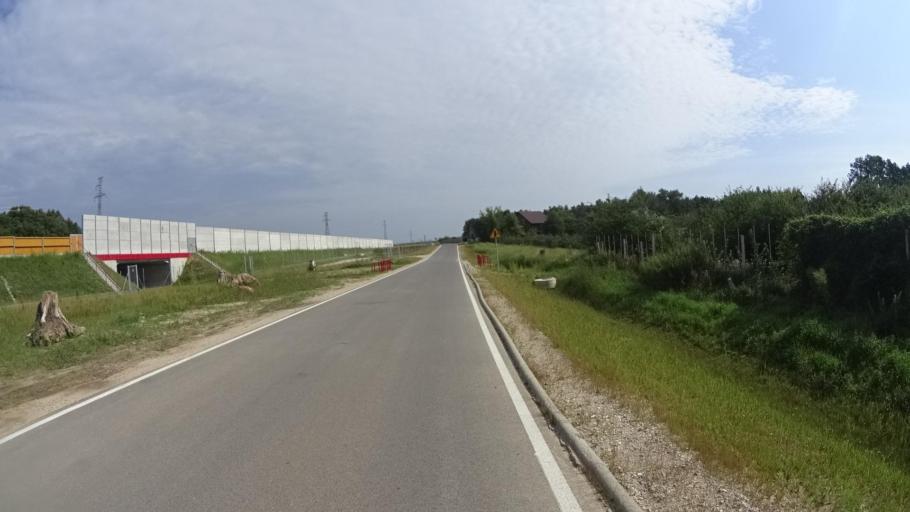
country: PL
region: Masovian Voivodeship
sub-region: Powiat piaseczynski
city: Tarczyn
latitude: 51.9613
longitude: 20.8561
